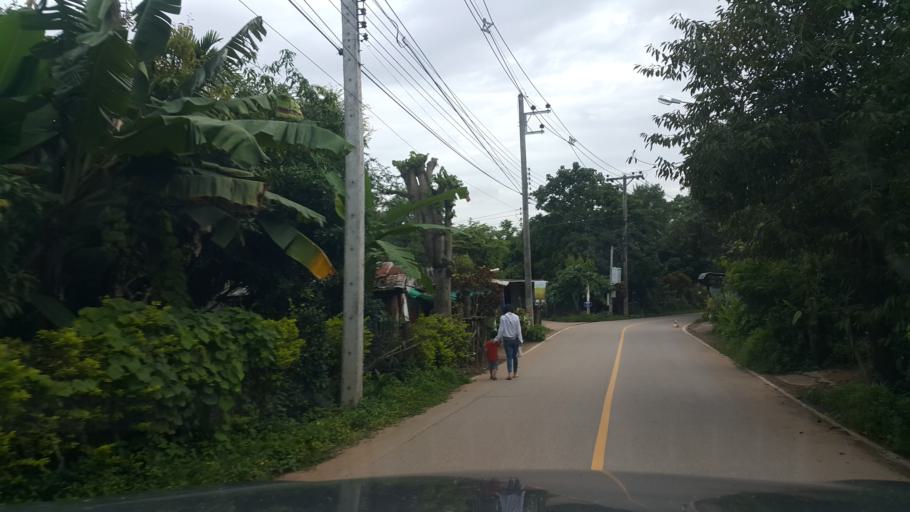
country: TH
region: Chiang Mai
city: San Sai
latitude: 18.9884
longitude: 99.1273
